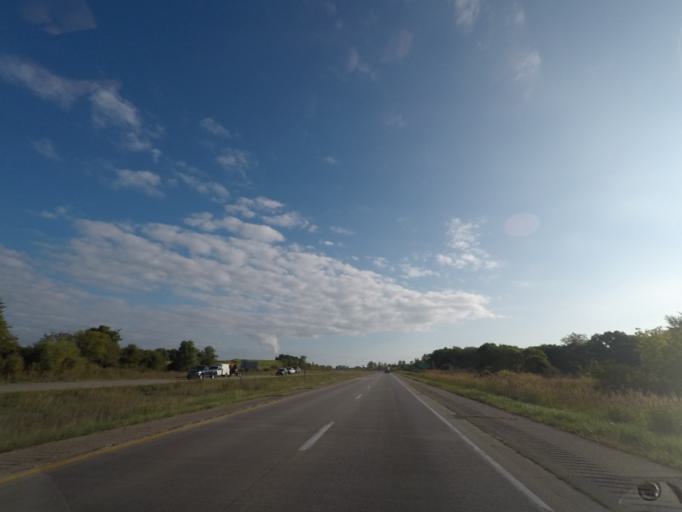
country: US
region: Iowa
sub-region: Polk County
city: Pleasant Hill
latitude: 41.5844
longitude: -93.5049
